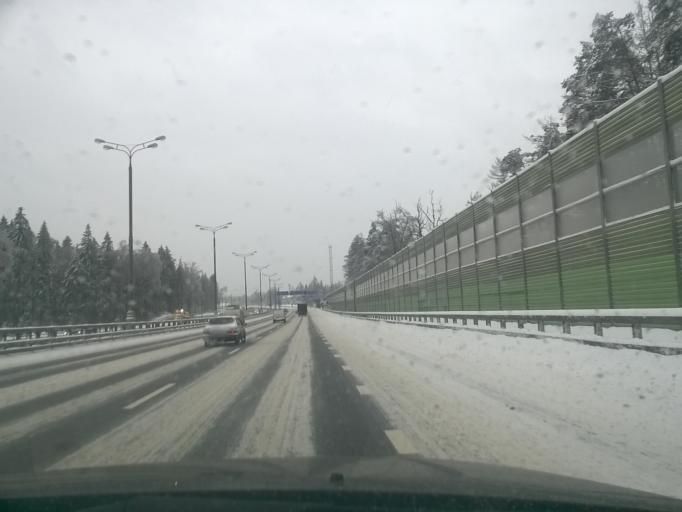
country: RU
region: Moskovskaya
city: Selyatino
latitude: 55.5211
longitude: 37.0060
